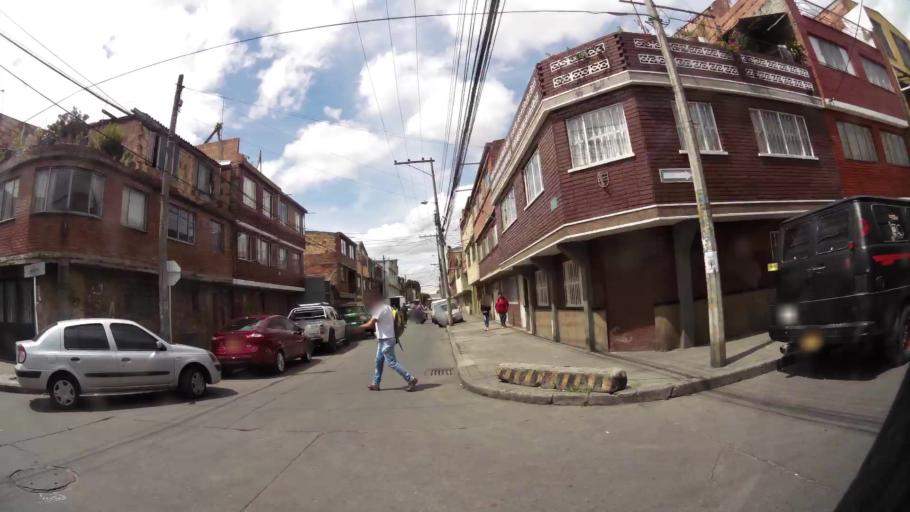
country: CO
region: Bogota D.C.
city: Bogota
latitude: 4.6944
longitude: -74.1137
